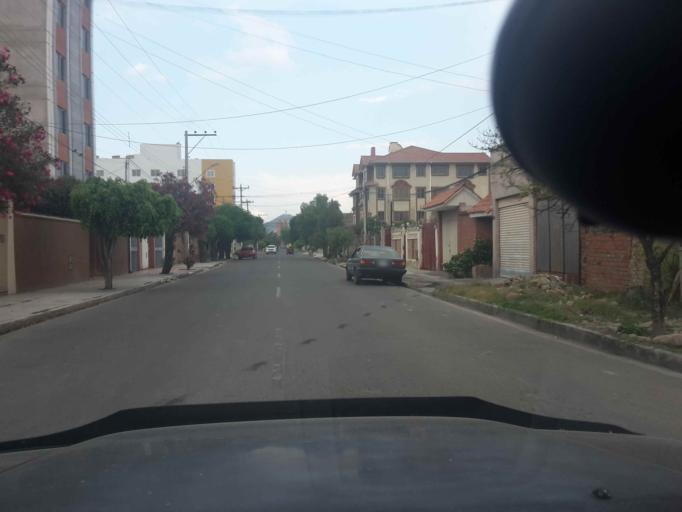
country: BO
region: Cochabamba
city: Cochabamba
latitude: -17.3804
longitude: -66.1848
